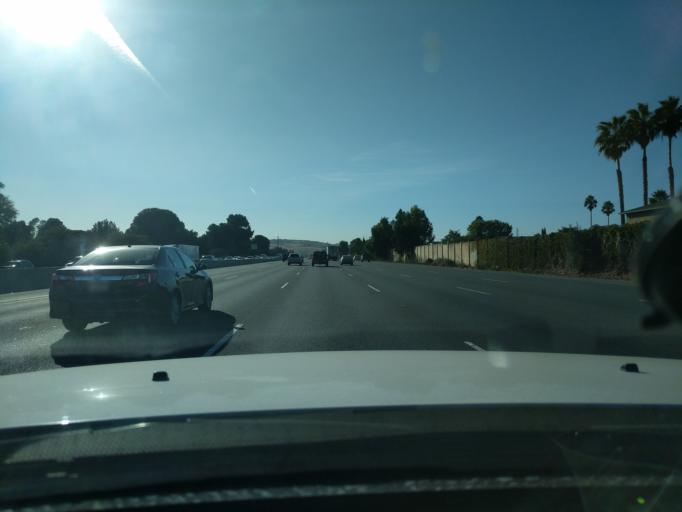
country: US
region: California
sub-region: Santa Clara County
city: Seven Trees
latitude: 37.3146
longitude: -121.8279
